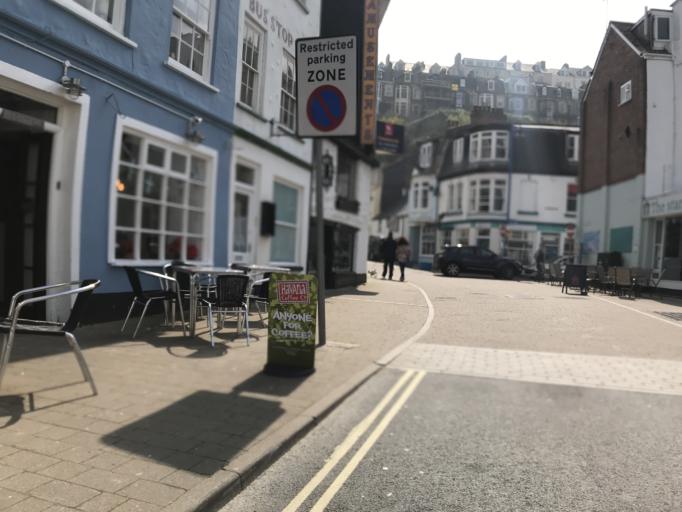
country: GB
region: England
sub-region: Devon
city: Ilfracombe
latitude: 51.2101
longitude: -4.1165
